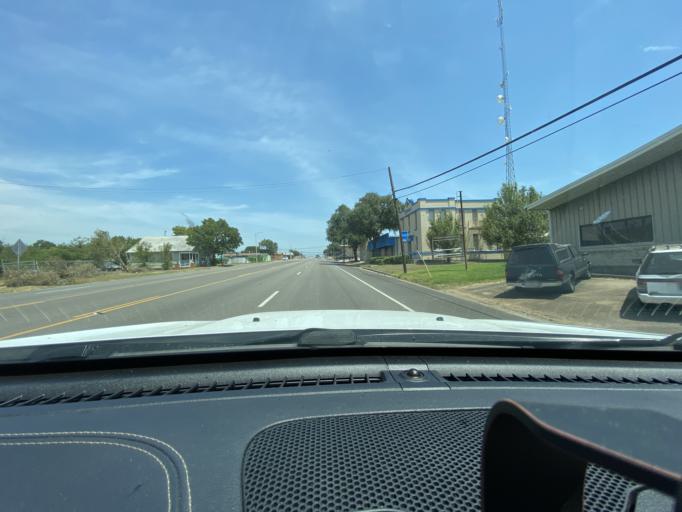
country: US
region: Texas
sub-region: Lee County
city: Giddings
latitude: 30.1794
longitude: -96.9381
